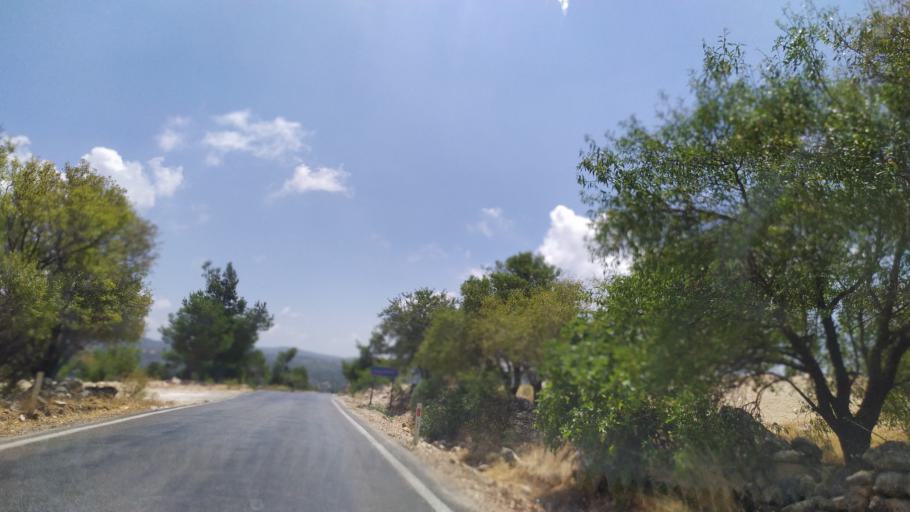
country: TR
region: Mersin
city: Gulnar
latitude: 36.2819
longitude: 33.3885
